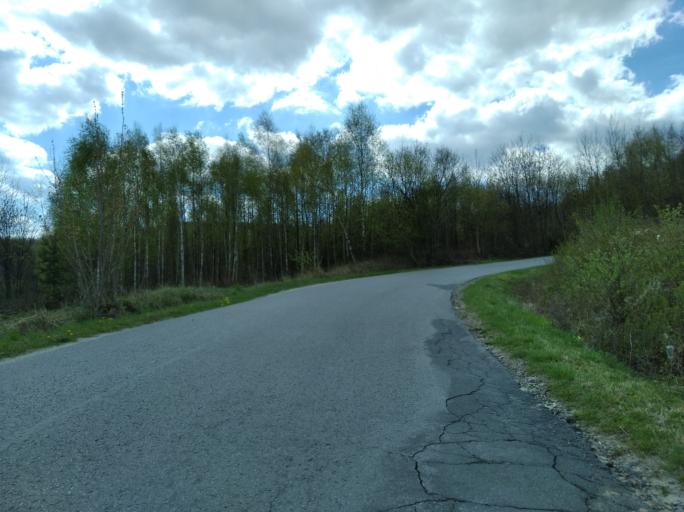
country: PL
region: Subcarpathian Voivodeship
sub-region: Powiat brzozowski
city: Wesola
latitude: 49.7721
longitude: 22.1333
